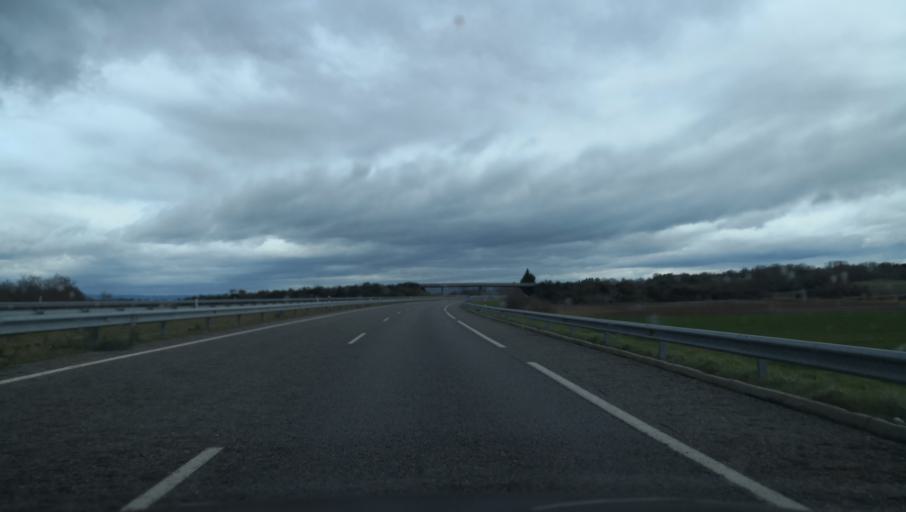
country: ES
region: Galicia
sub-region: Provincia de Ourense
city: Trasmiras
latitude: 42.0310
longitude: -7.6522
